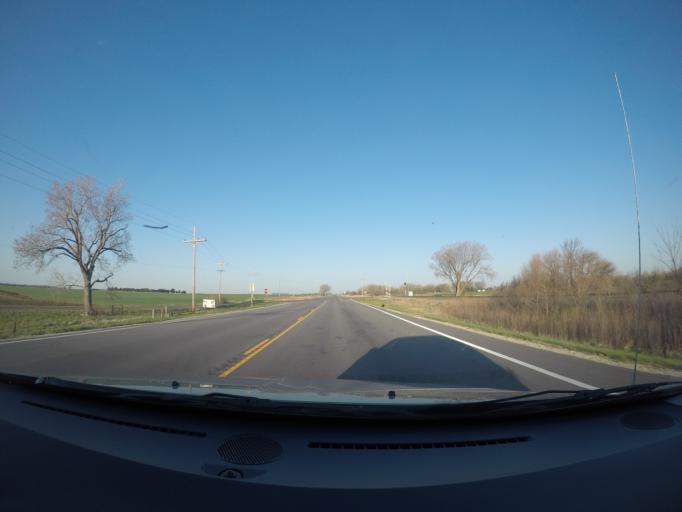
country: US
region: Kansas
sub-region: Stafford County
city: Stafford
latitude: 37.8063
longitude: -98.4413
